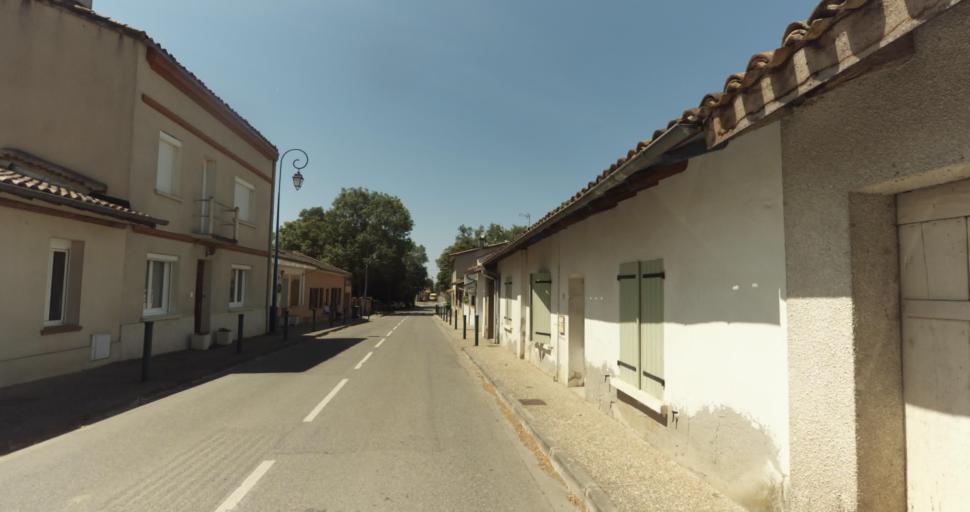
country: FR
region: Midi-Pyrenees
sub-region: Departement de la Haute-Garonne
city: Levignac
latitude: 43.6390
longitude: 1.1686
